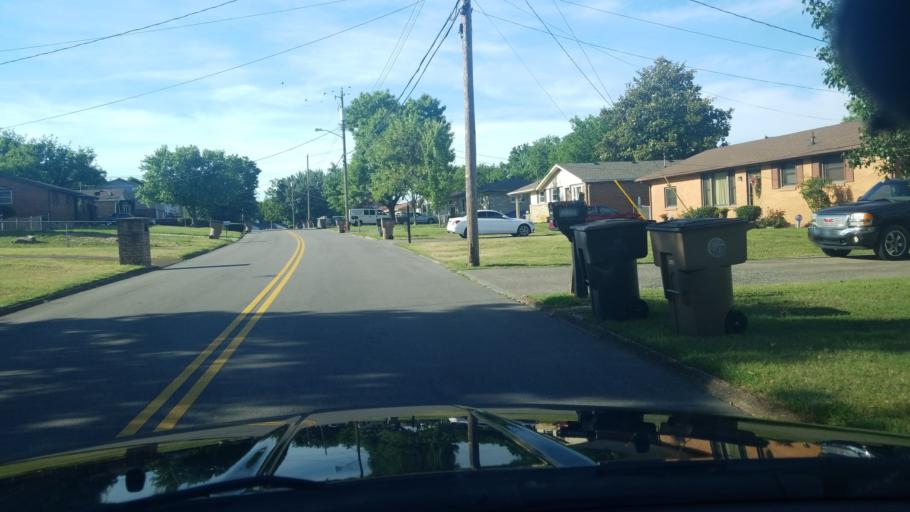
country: US
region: Tennessee
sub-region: Davidson County
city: Nashville
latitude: 36.2345
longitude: -86.7732
